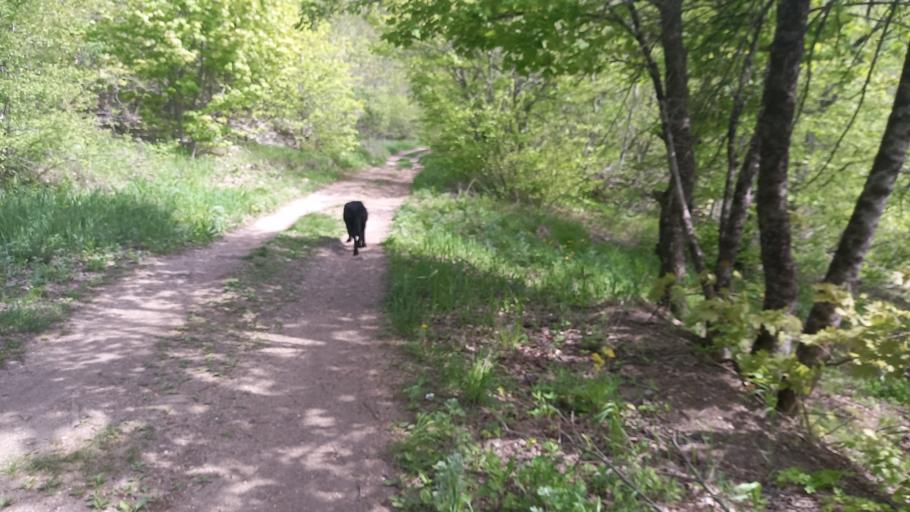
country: RU
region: Stavropol'skiy
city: Pyatigorsk
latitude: 44.0892
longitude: 43.0296
